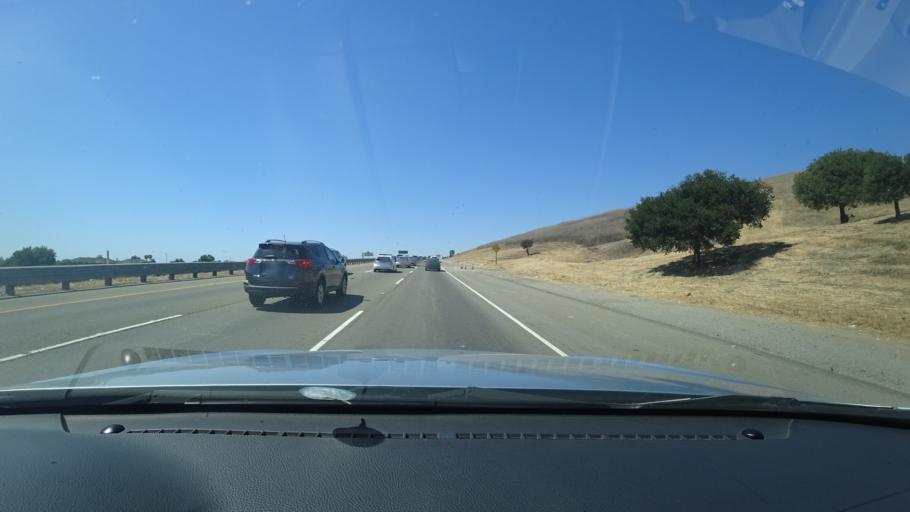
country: US
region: California
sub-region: Santa Clara County
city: Milpitas
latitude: 37.4781
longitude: -121.9117
